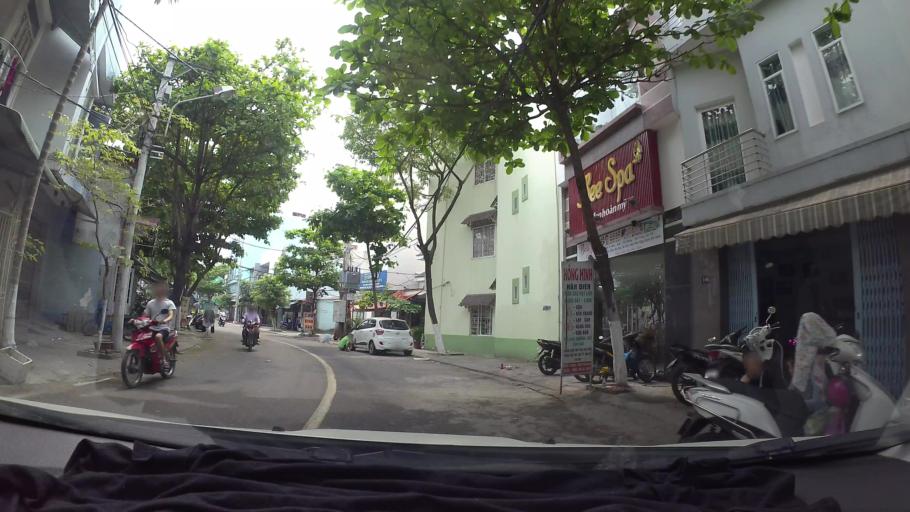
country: VN
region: Da Nang
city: Da Nang
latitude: 16.0836
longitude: 108.2158
